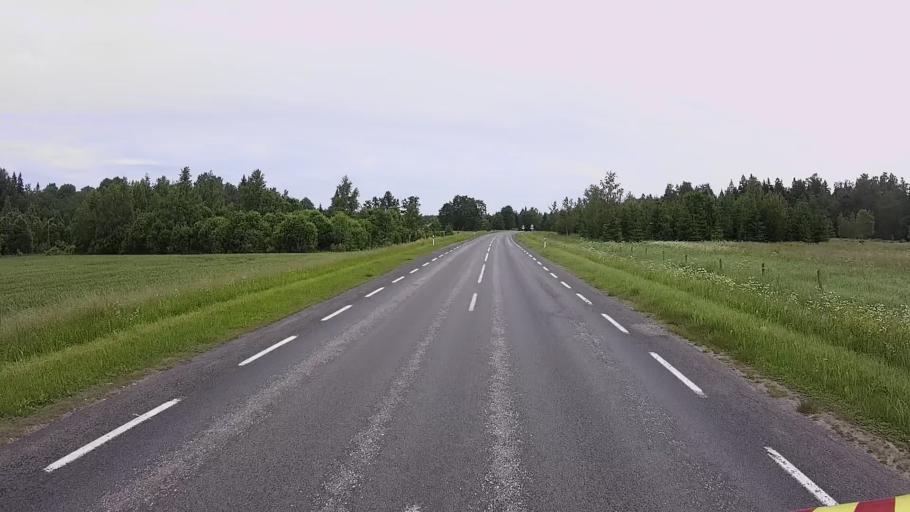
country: EE
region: Viljandimaa
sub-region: Karksi vald
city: Karksi-Nuia
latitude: 58.1811
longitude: 25.5919
